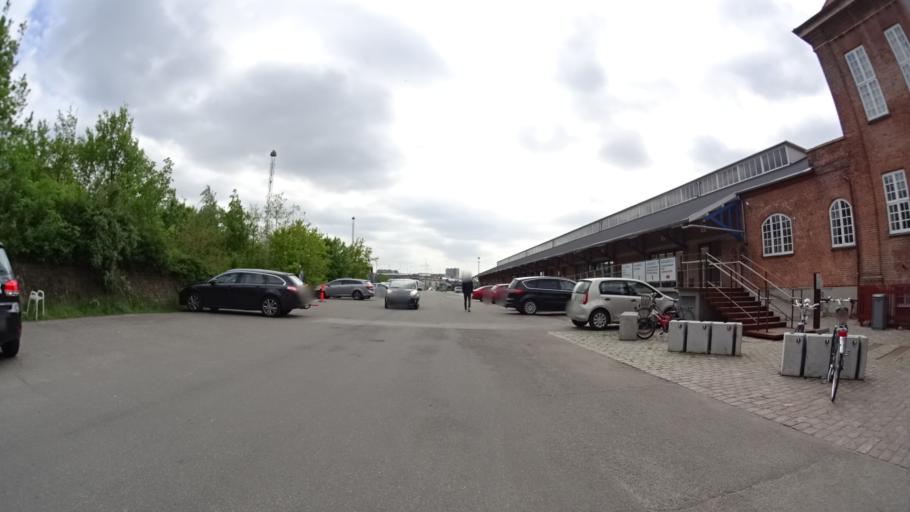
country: DK
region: Central Jutland
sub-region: Arhus Kommune
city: Arhus
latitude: 56.1539
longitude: 10.1956
